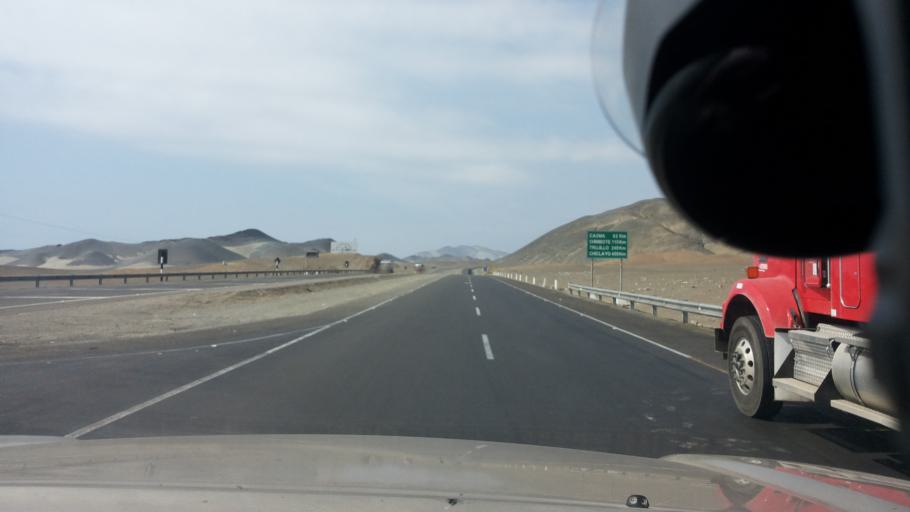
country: PE
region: Ancash
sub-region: Provincia de Huarmey
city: La Caleta Culebras
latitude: -9.9228
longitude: -78.2200
